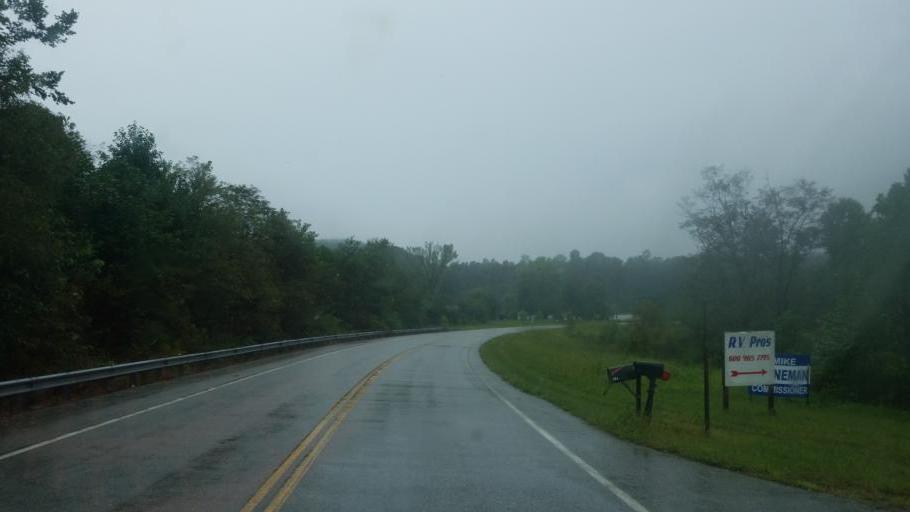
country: US
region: Kentucky
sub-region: Greenup County
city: South Shore
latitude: 38.6754
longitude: -82.9258
